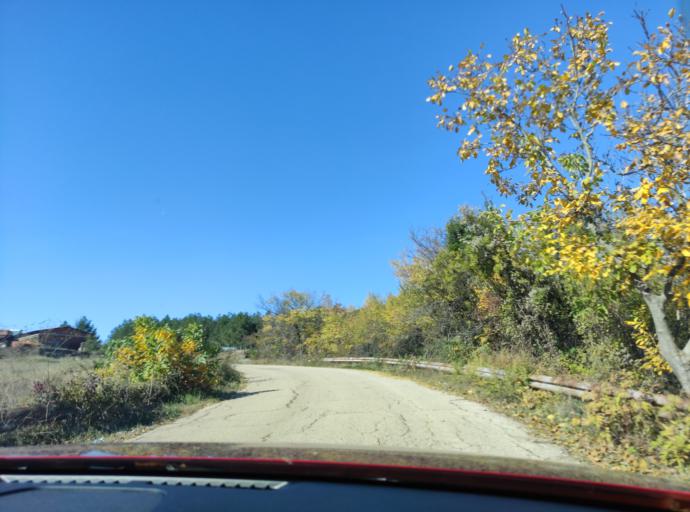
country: BG
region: Montana
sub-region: Obshtina Chiprovtsi
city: Chiprovtsi
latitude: 43.4559
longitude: 23.0474
